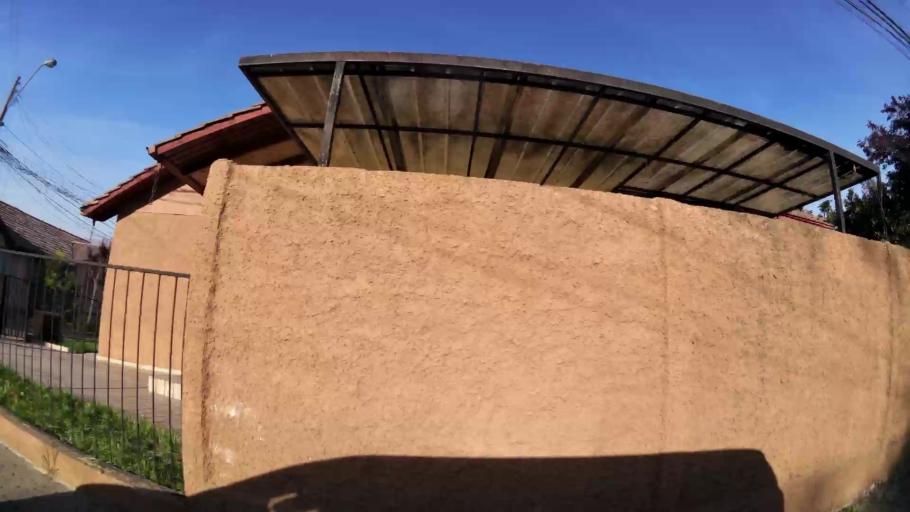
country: CL
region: Santiago Metropolitan
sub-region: Provincia de Cordillera
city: Puente Alto
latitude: -33.5429
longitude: -70.5766
